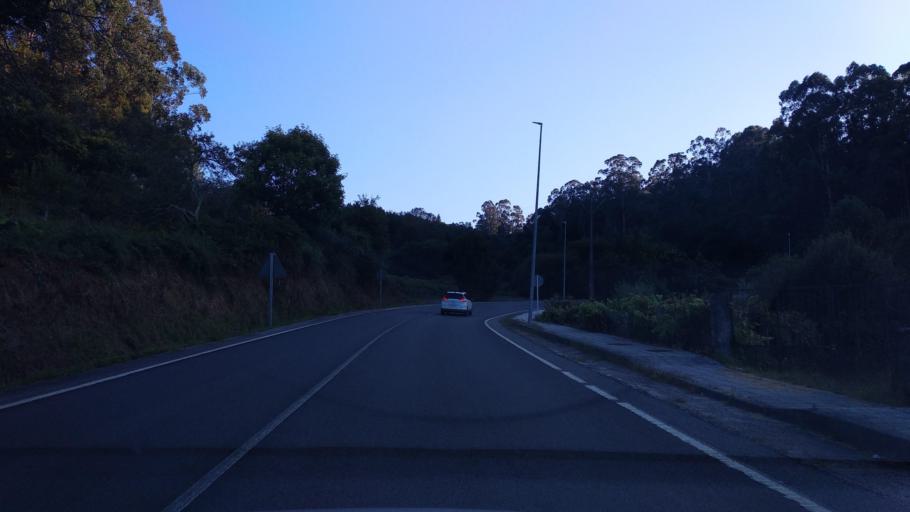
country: ES
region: Galicia
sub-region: Provincia de Pontevedra
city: Redondela
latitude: 42.3349
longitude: -8.5800
